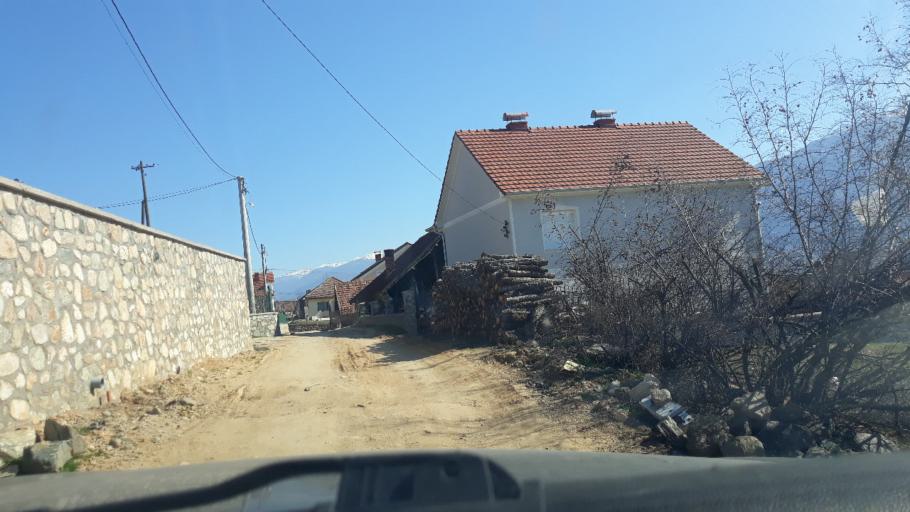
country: MK
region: Novo Selo
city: Novo Selo
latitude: 41.4183
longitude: 22.8810
